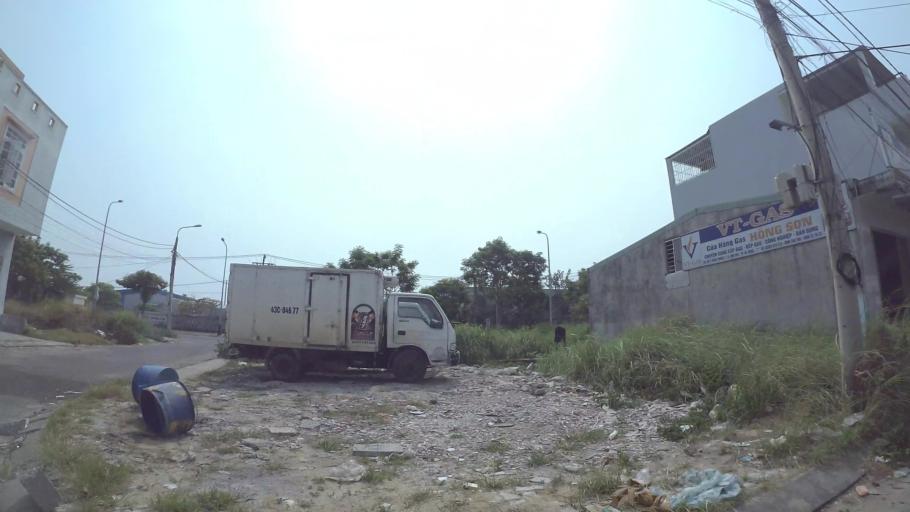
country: VN
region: Da Nang
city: Da Nang
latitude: 16.0939
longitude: 108.2385
